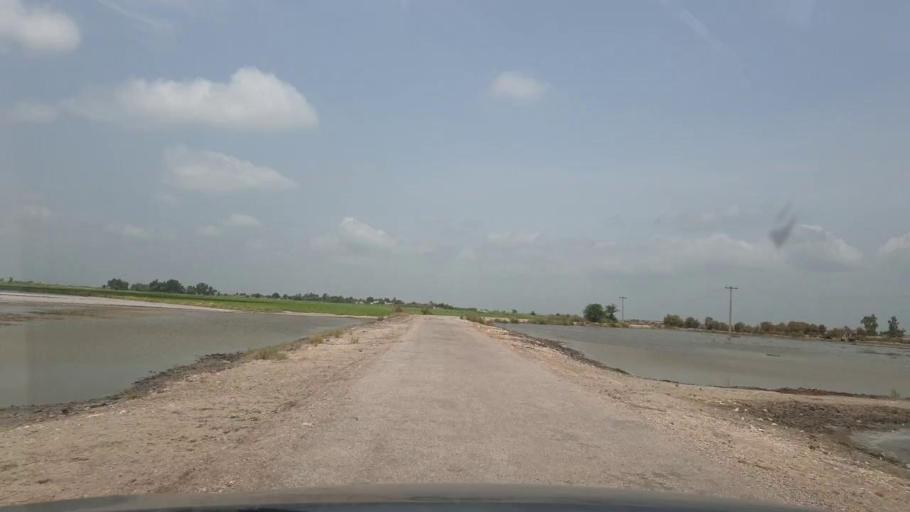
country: PK
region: Sindh
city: Ratodero
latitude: 27.9042
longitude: 68.3148
